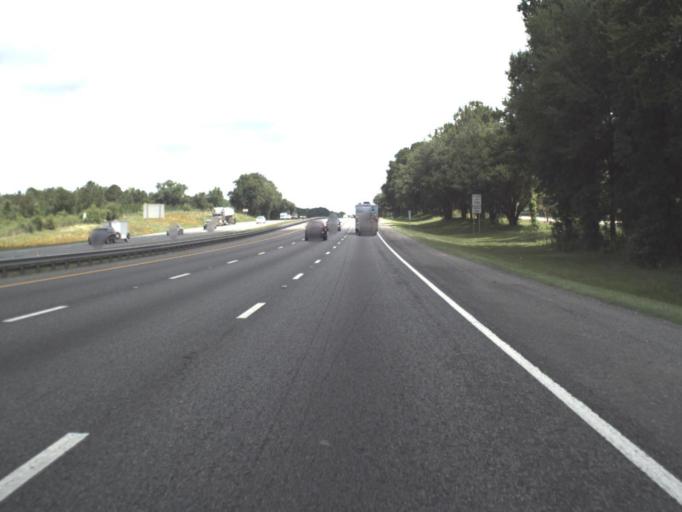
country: US
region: Florida
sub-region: Columbia County
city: Lake City
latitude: 30.1860
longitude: -82.6916
